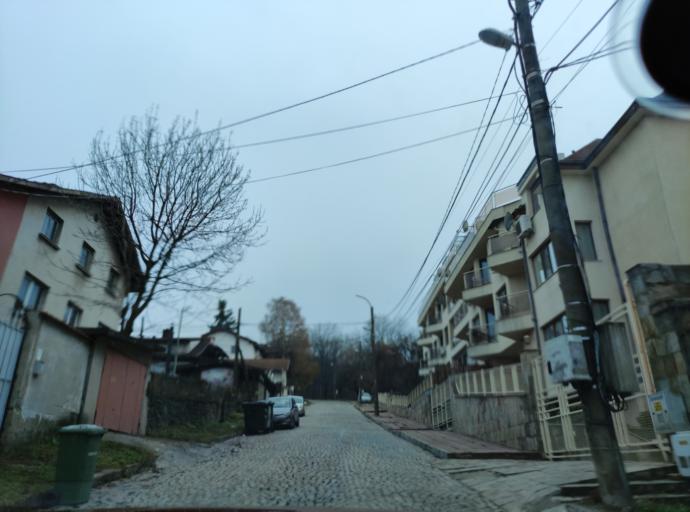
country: BG
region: Sofia-Capital
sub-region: Stolichna Obshtina
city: Sofia
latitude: 42.6276
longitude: 23.3084
